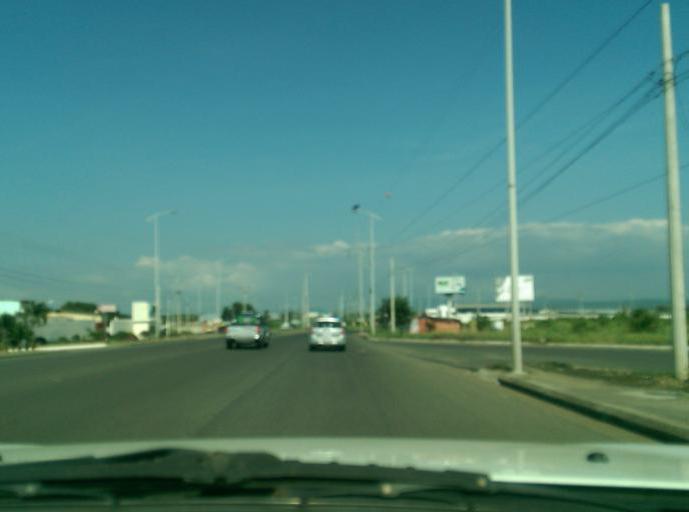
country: EC
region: Manabi
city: Manta
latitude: -0.9644
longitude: -80.6702
